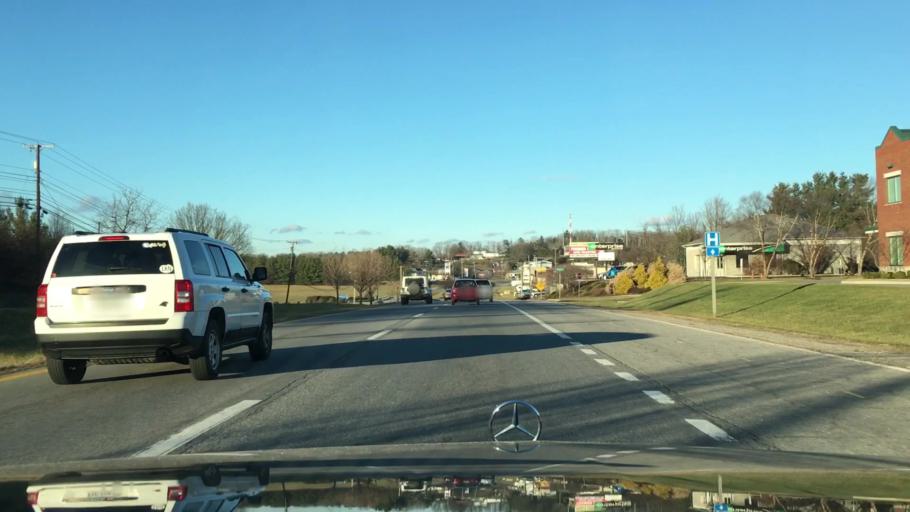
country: US
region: Virginia
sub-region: Montgomery County
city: Merrimac
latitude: 37.1698
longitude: -80.4211
